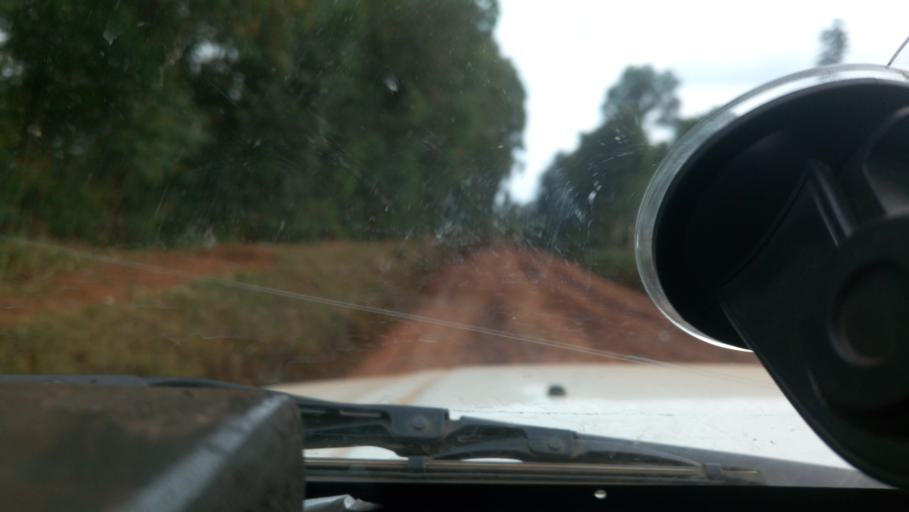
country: KE
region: Nyamira District
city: Keroka
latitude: -0.8176
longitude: 34.8992
